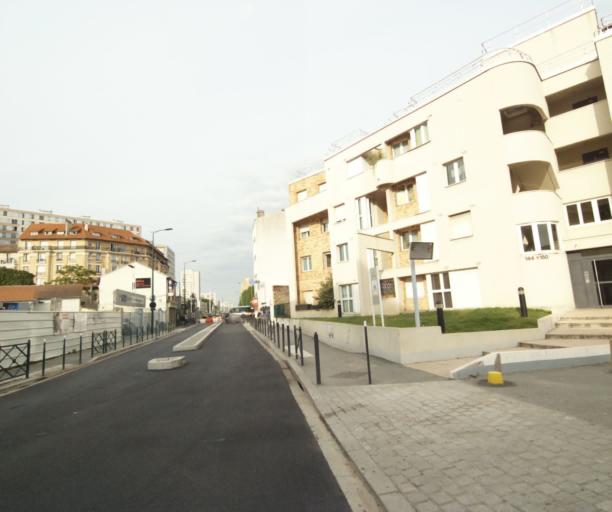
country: FR
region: Ile-de-France
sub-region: Departement des Hauts-de-Seine
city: Clichy
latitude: 48.8753
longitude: 2.3136
